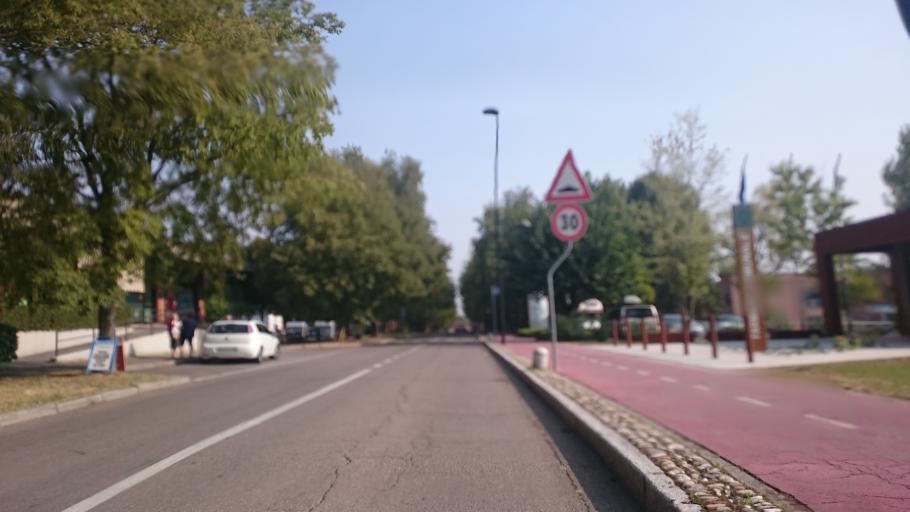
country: IT
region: Emilia-Romagna
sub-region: Provincia di Reggio Emilia
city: Albinea
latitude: 44.6272
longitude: 10.6118
